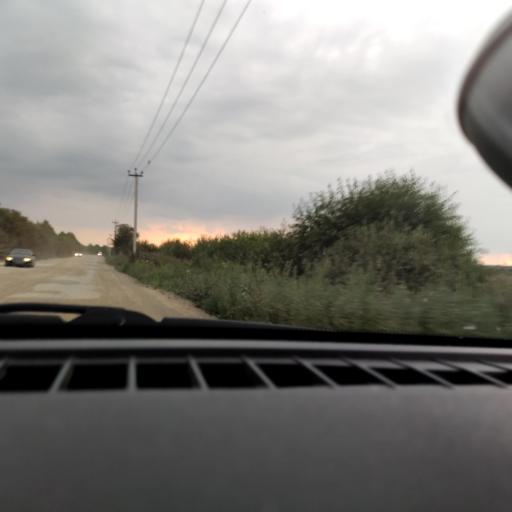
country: RU
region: Perm
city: Kondratovo
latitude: 58.0039
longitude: 56.0255
